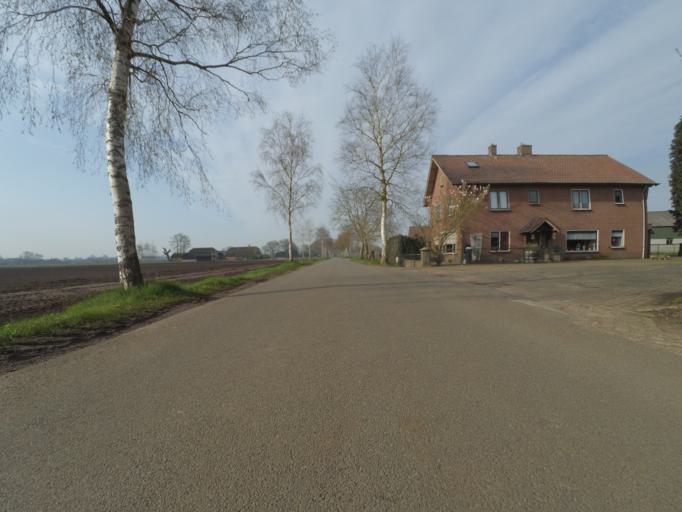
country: NL
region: Gelderland
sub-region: Gemeente Barneveld
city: Stroe
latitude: 52.1664
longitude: 5.6989
